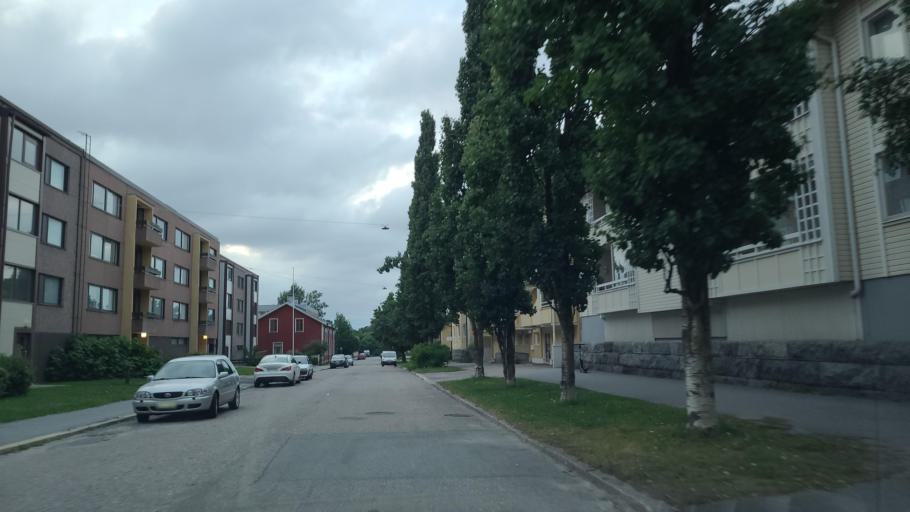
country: FI
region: Ostrobothnia
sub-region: Vaasa
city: Vaasa
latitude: 63.1021
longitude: 21.6169
